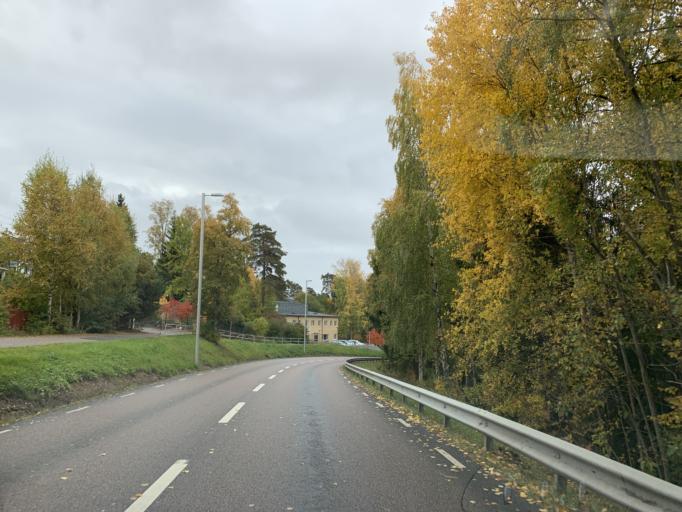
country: SE
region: Stockholm
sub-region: Botkyrka Kommun
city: Varsta
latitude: 59.1674
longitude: 17.7980
